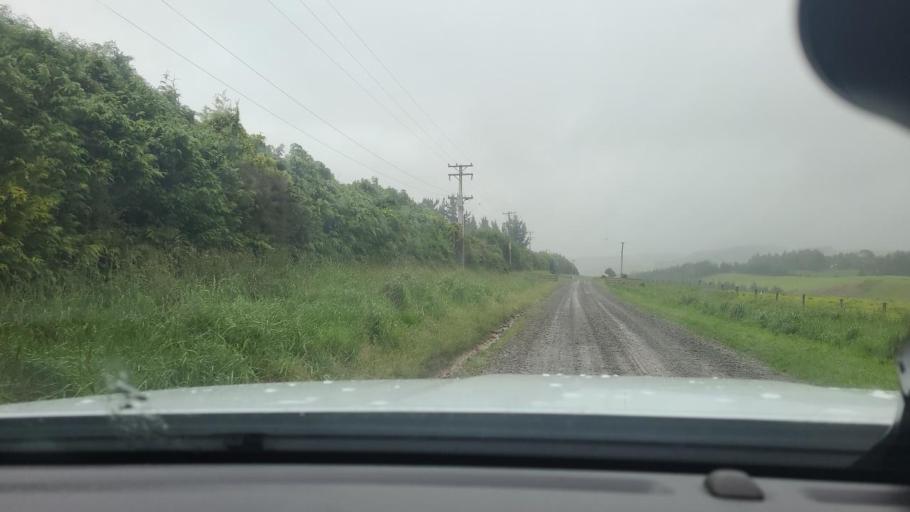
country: NZ
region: Southland
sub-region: Southland District
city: Riverton
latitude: -45.9806
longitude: 167.9557
